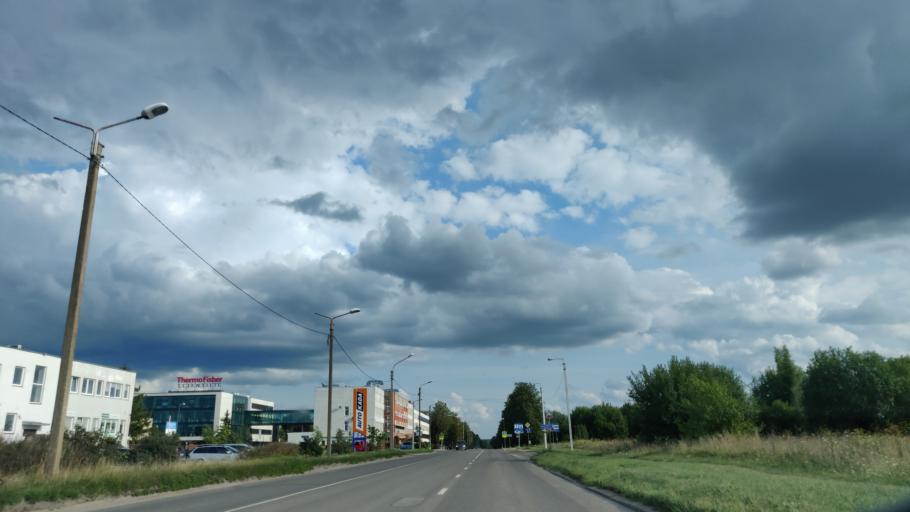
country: LT
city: Baltoji Voke
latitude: 54.6262
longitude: 25.1395
